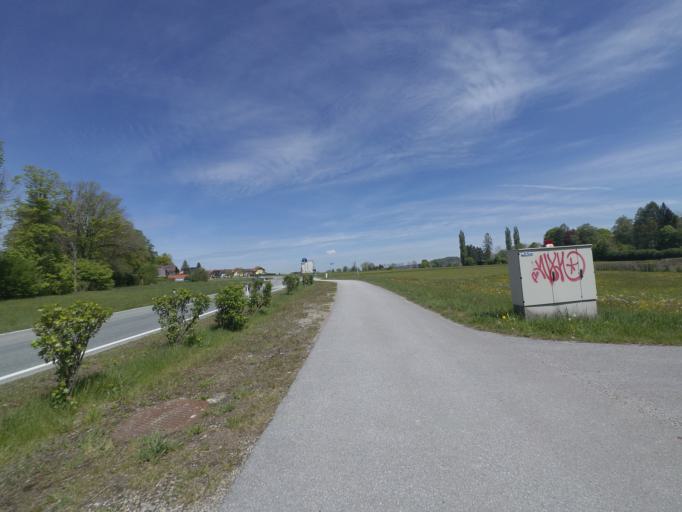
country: AT
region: Salzburg
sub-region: Politischer Bezirk Salzburg-Umgebung
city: Seeham
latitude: 47.9549
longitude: 13.0732
